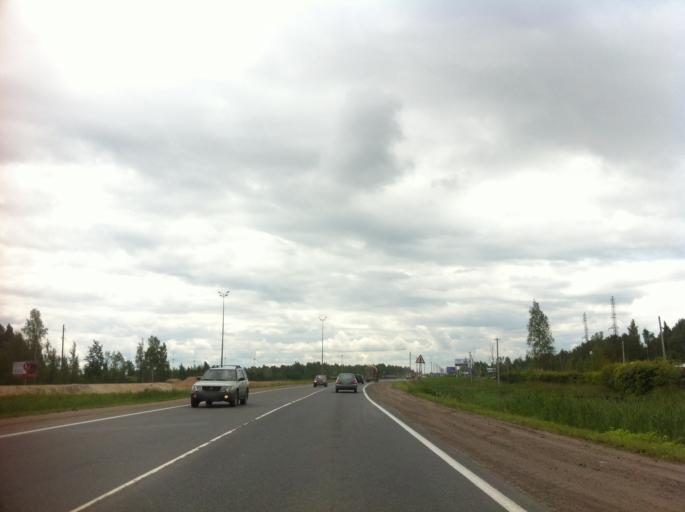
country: RU
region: Leningrad
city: Maloye Verevo
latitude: 59.5770
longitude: 30.1702
